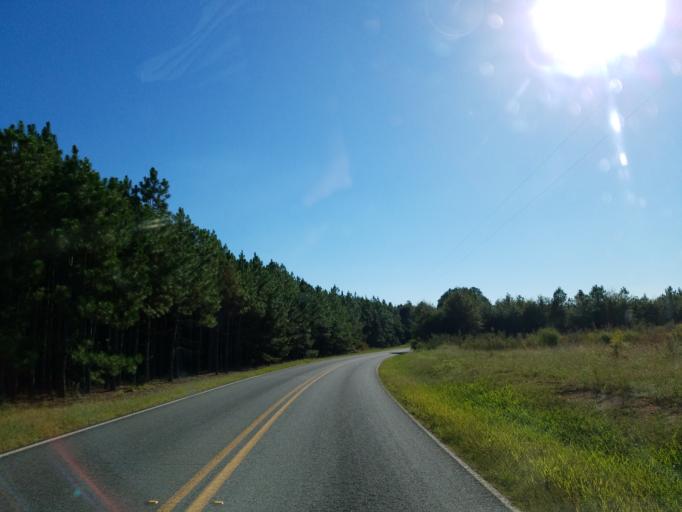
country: US
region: Georgia
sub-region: Dooly County
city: Unadilla
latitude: 32.2188
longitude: -83.8856
